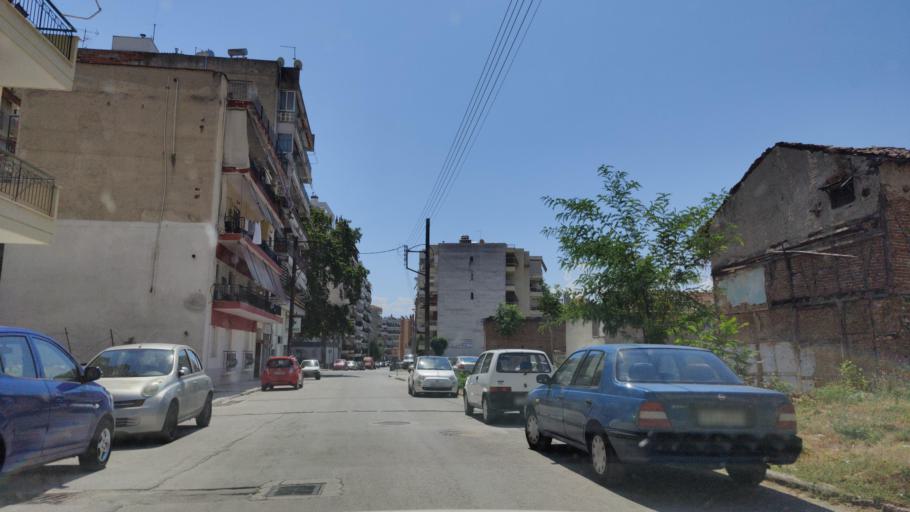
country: GR
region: Central Macedonia
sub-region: Nomos Serron
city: Serres
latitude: 41.0877
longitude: 23.5376
